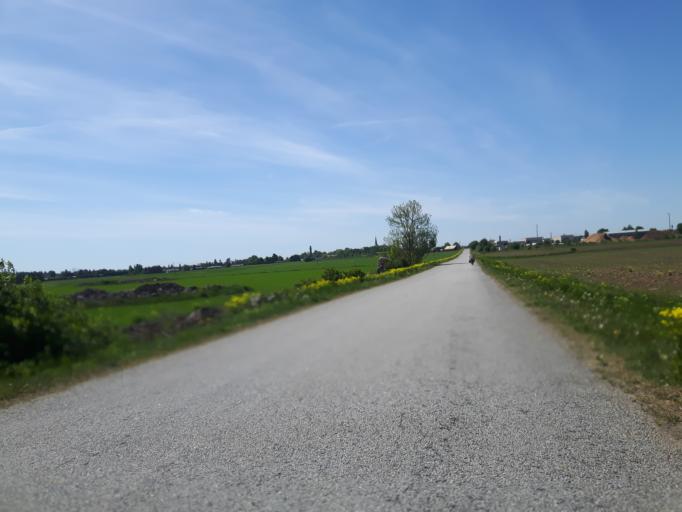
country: EE
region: Ida-Virumaa
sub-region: Aseri vald
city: Aseri
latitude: 59.4544
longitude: 26.7037
